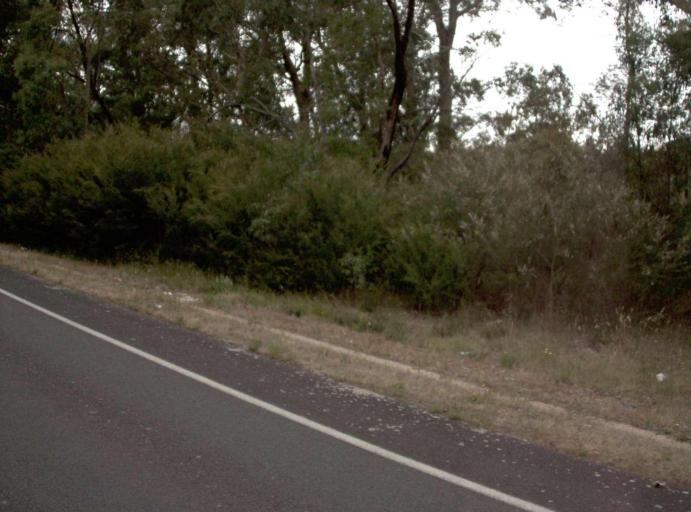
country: AU
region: Victoria
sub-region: Latrobe
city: Traralgon
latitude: -38.5436
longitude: 146.8350
